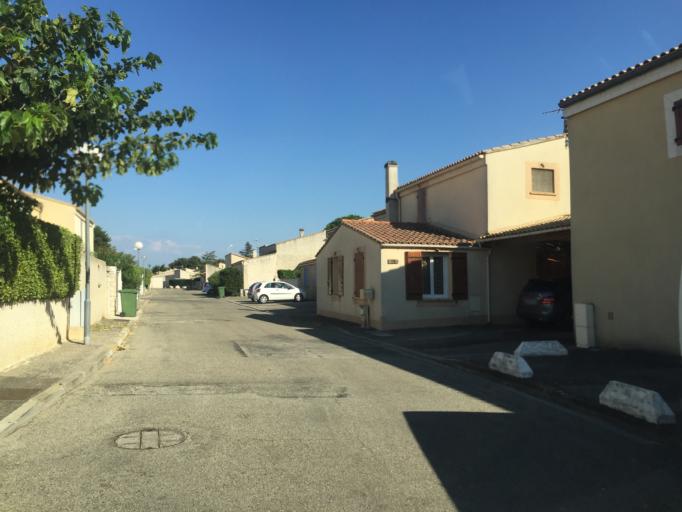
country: FR
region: Provence-Alpes-Cote d'Azur
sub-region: Departement du Vaucluse
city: Sorgues
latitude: 44.0235
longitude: 4.8574
